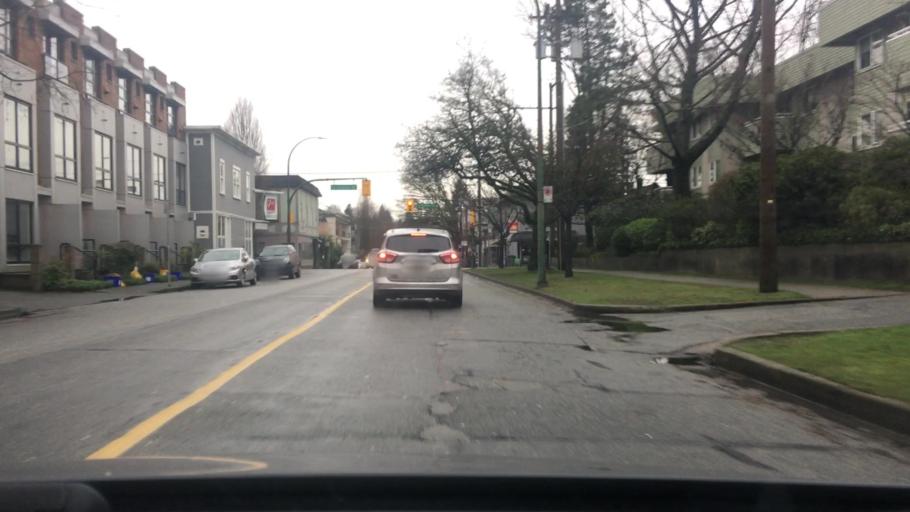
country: CA
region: British Columbia
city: Vancouver
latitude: 49.2570
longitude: -123.1190
